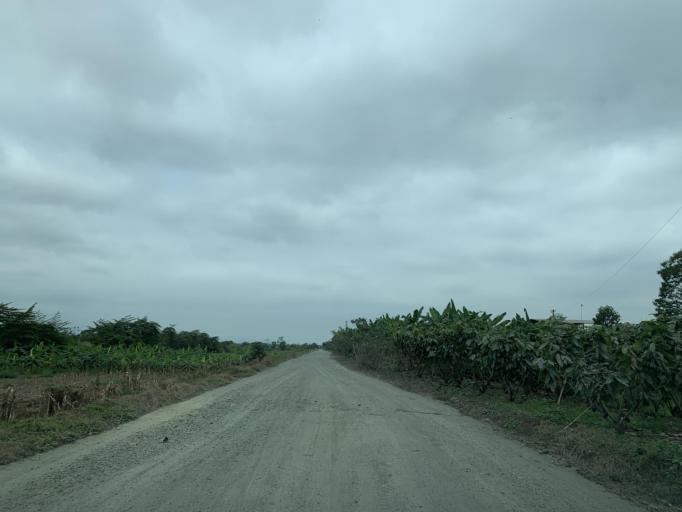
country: EC
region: Canar
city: La Troncal
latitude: -2.3710
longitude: -79.4205
